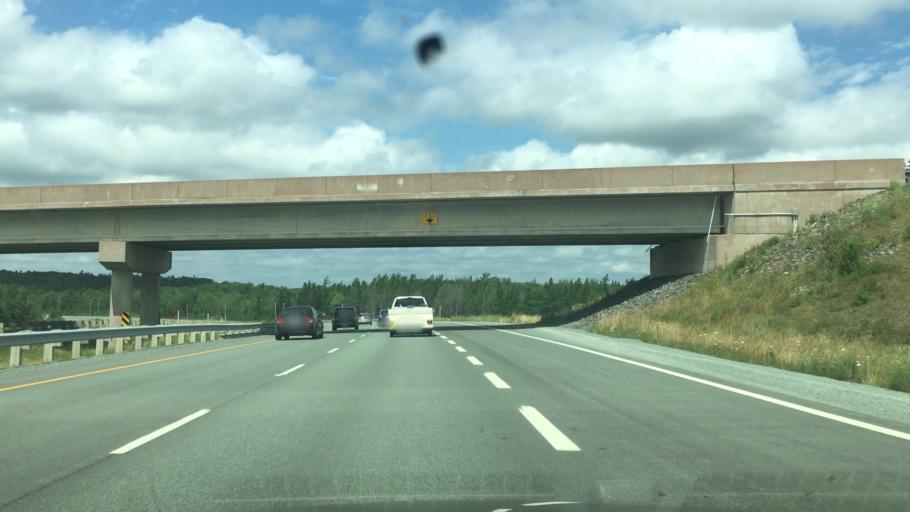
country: CA
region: Nova Scotia
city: Oxford
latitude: 45.6949
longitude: -63.7758
